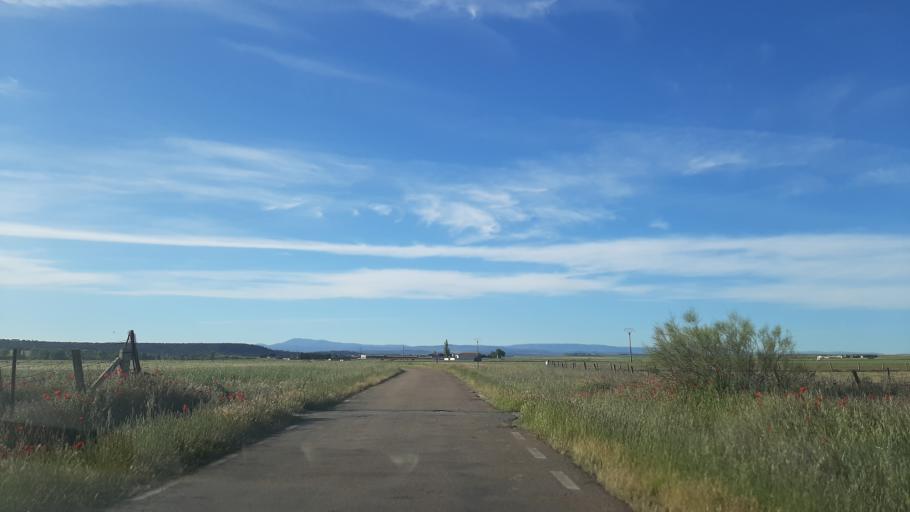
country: ES
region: Castille and Leon
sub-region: Provincia de Salamanca
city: Pedrosillo de Alba
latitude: 40.8168
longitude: -5.3897
